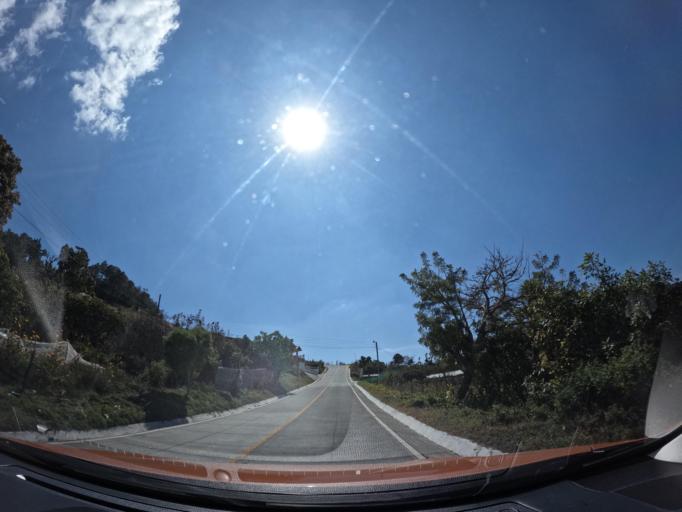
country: GT
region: Solola
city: San Antonio Palopo
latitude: 14.6925
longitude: -91.0756
